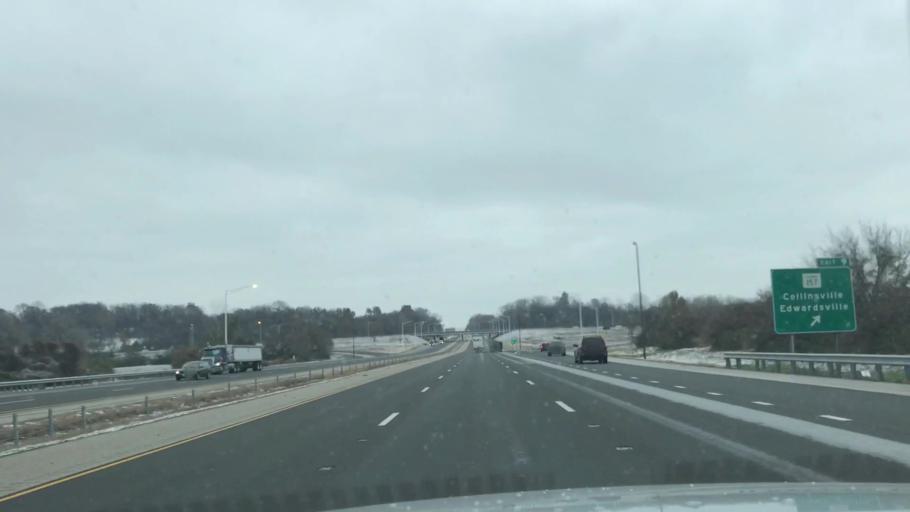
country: US
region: Illinois
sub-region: Madison County
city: Glen Carbon
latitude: 38.7566
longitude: -90.0149
